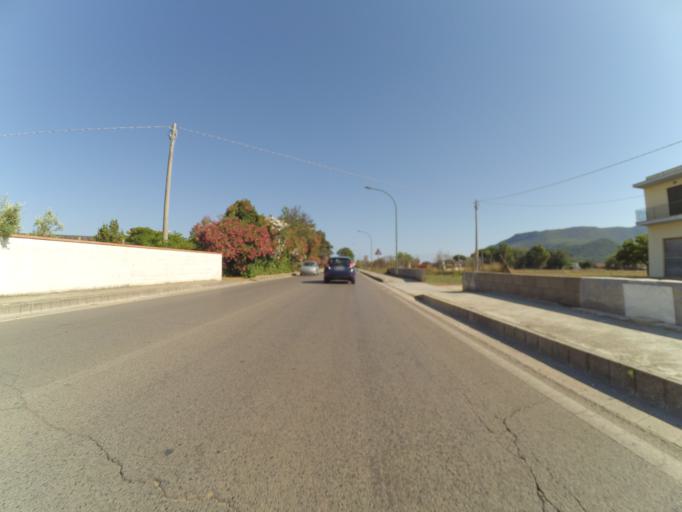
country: IT
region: Latium
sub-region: Provincia di Latina
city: San Felice Circeo
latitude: 41.2554
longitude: 13.0928
